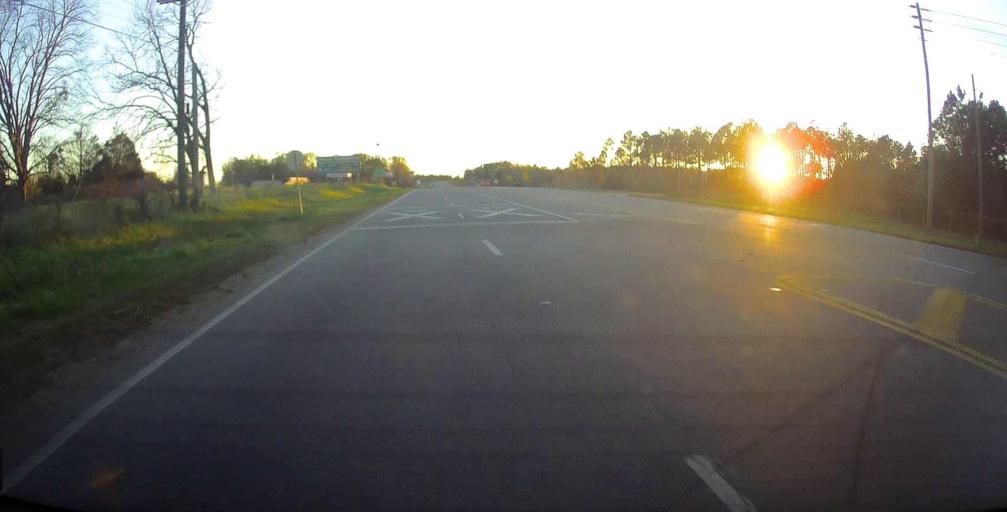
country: US
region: Georgia
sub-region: Crisp County
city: Cordele
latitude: 31.9617
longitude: -83.7990
